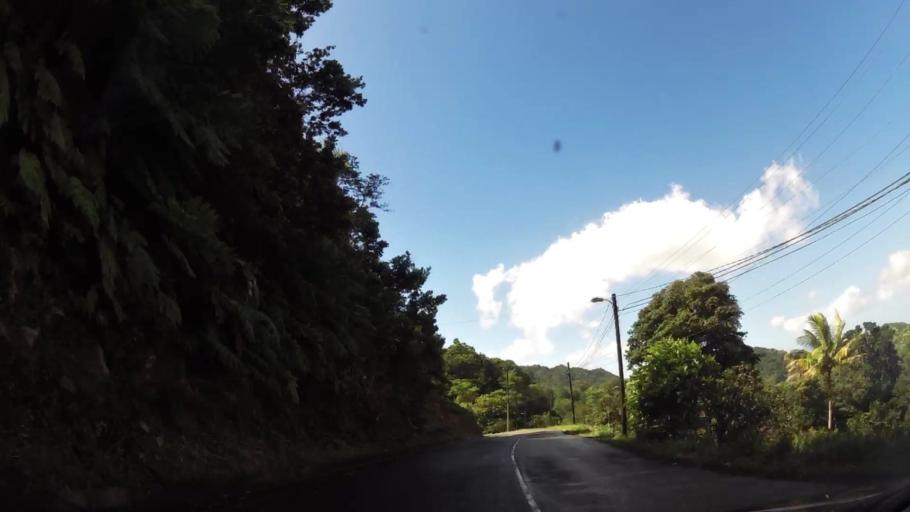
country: DM
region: Saint Paul
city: Pont Casse
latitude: 15.3720
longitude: -61.3481
